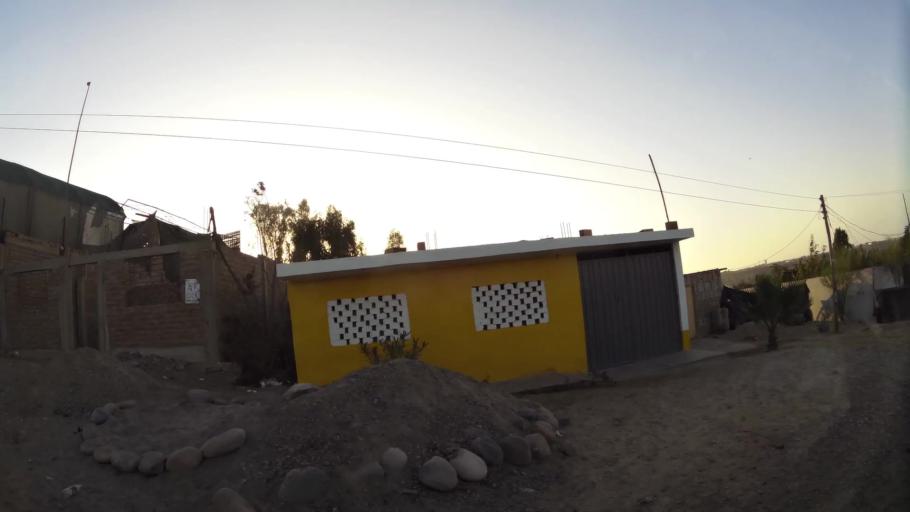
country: PE
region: Ica
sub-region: Provincia de Pisco
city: Villa Tupac Amaru
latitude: -13.6991
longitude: -76.1531
